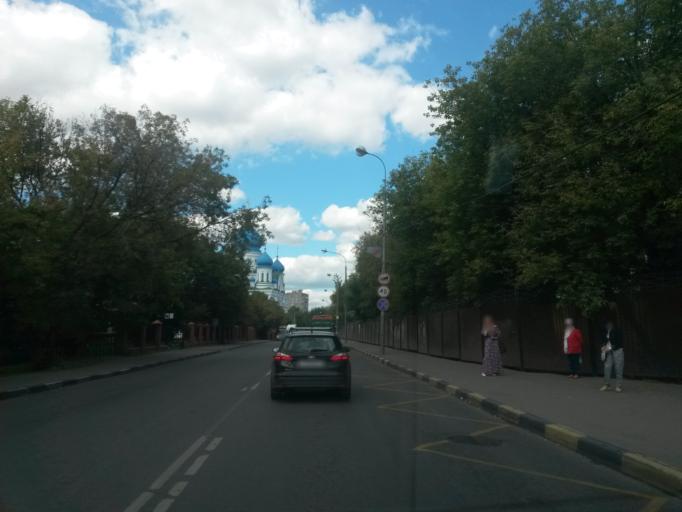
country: RU
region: Moscow
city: Mar'ino
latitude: 55.6667
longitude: 37.7202
